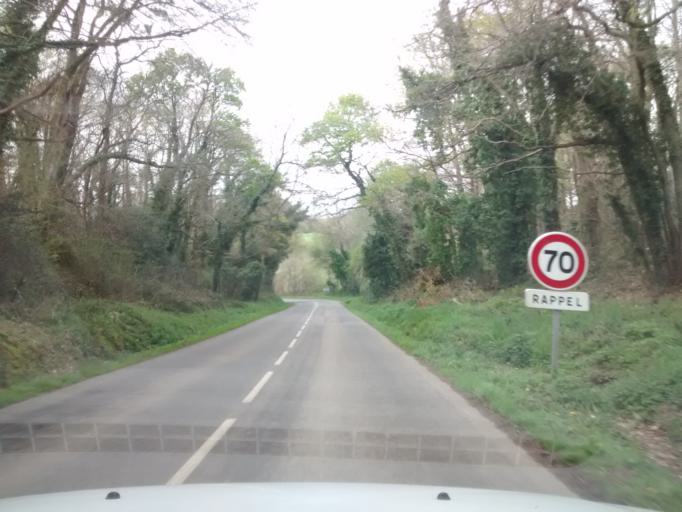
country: FR
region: Brittany
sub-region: Departement du Morbihan
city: Guidel-Plage
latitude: 47.7882
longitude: -3.5493
